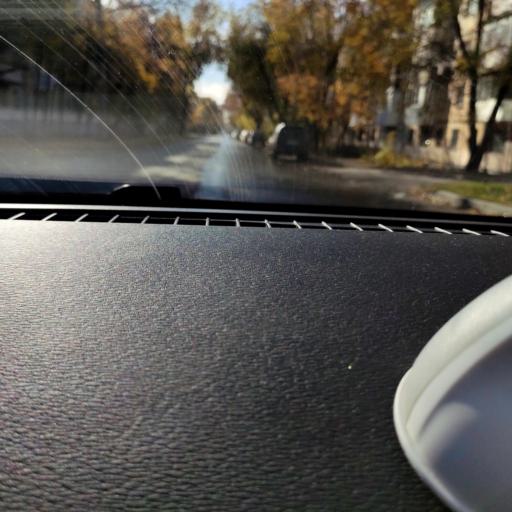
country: RU
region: Samara
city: Samara
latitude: 53.1957
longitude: 50.1737
